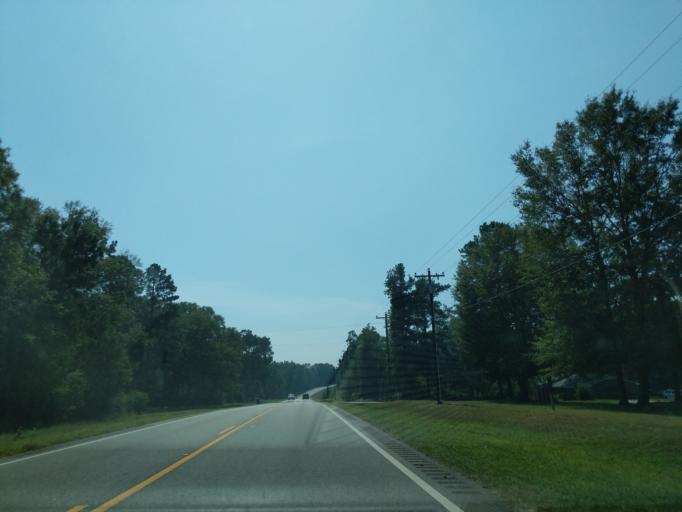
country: US
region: Alabama
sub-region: Covington County
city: Andalusia
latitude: 31.2581
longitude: -86.5170
